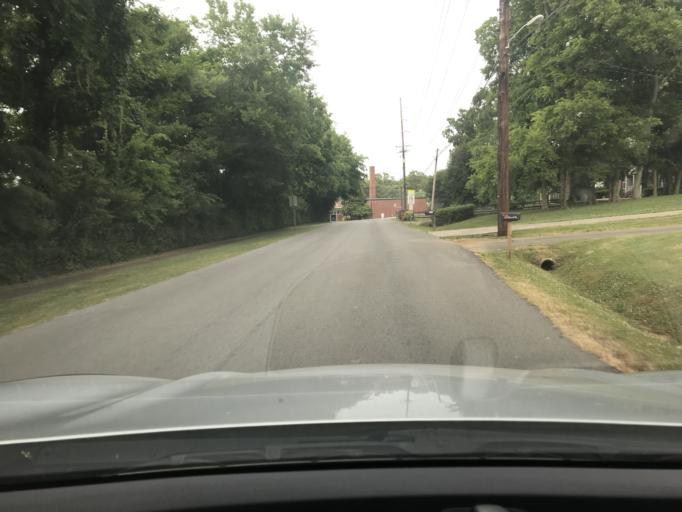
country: US
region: Tennessee
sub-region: Davidson County
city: Goodlettsville
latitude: 36.3129
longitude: -86.7125
